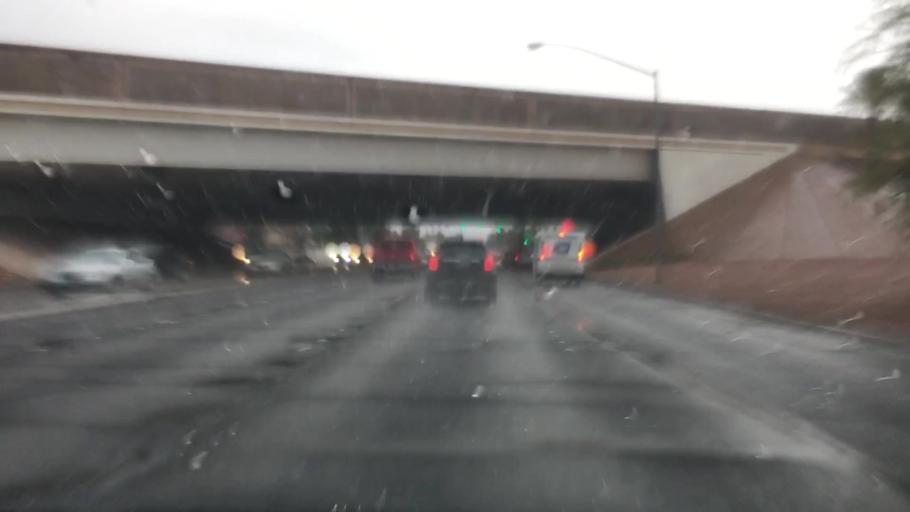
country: US
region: Nevada
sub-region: Clark County
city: Paradise
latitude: 36.0574
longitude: -115.1394
